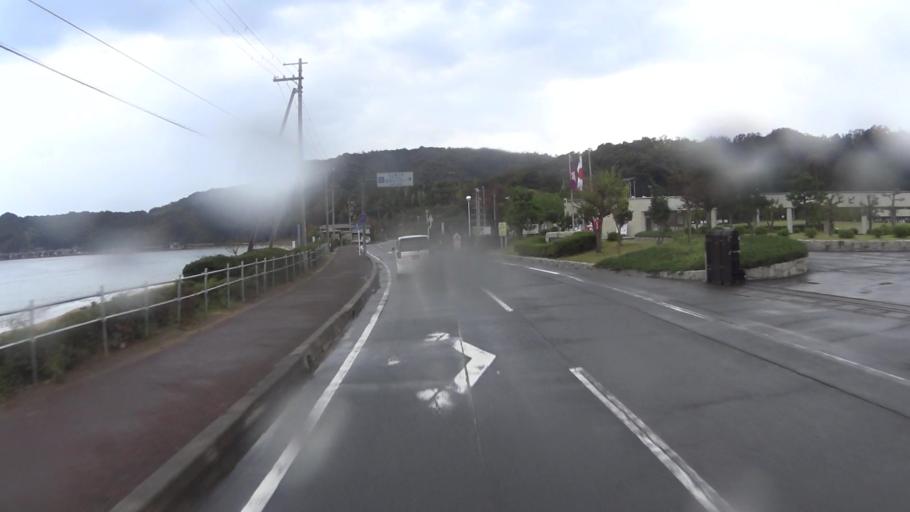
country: JP
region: Kyoto
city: Miyazu
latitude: 35.5832
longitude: 135.2311
